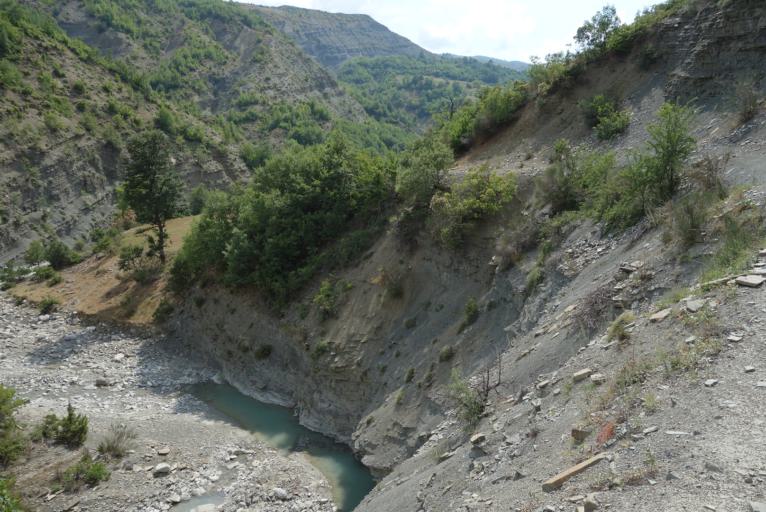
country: AL
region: Gjirokaster
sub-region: Rrethi i Permetit
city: Frasher
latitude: 40.3809
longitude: 20.3956
